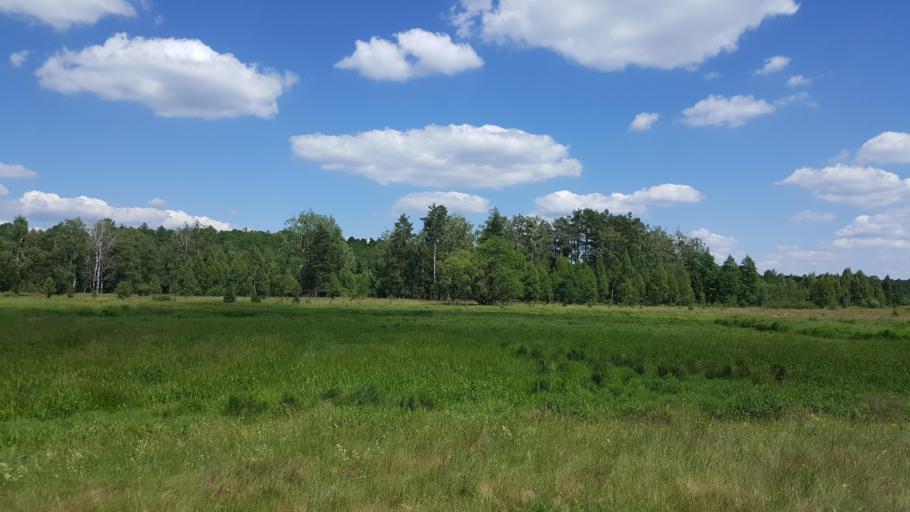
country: BY
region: Brest
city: Kamyanyuki
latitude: 52.5779
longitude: 23.7557
